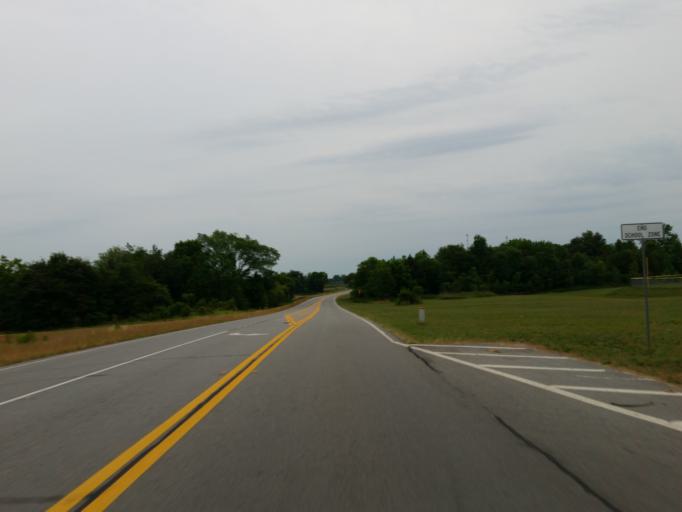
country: US
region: Georgia
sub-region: Dooly County
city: Unadilla
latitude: 32.1832
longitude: -83.7650
